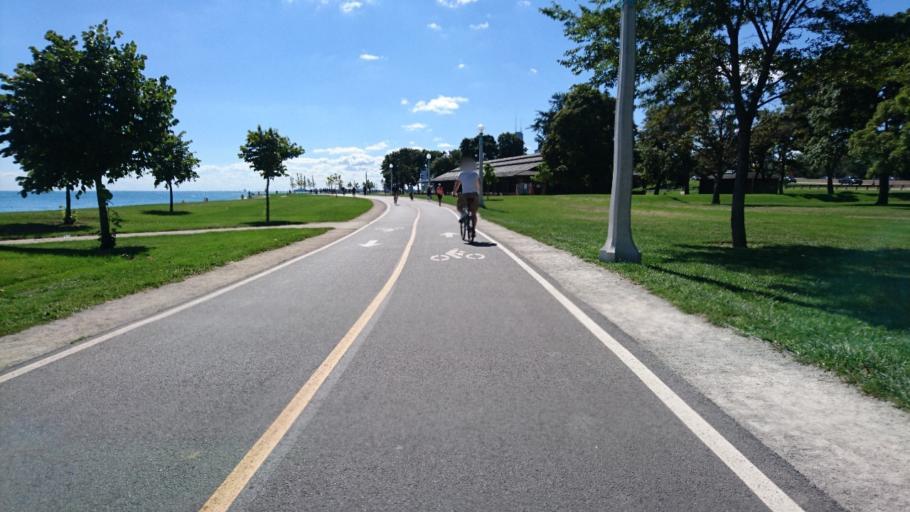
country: US
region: Illinois
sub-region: Cook County
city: Chicago
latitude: 41.9285
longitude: -87.6311
